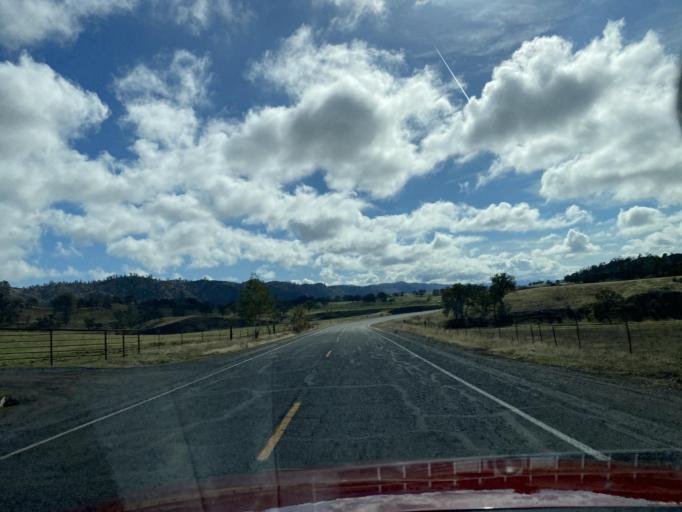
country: US
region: California
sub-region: Glenn County
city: Willows
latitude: 39.5448
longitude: -122.5369
